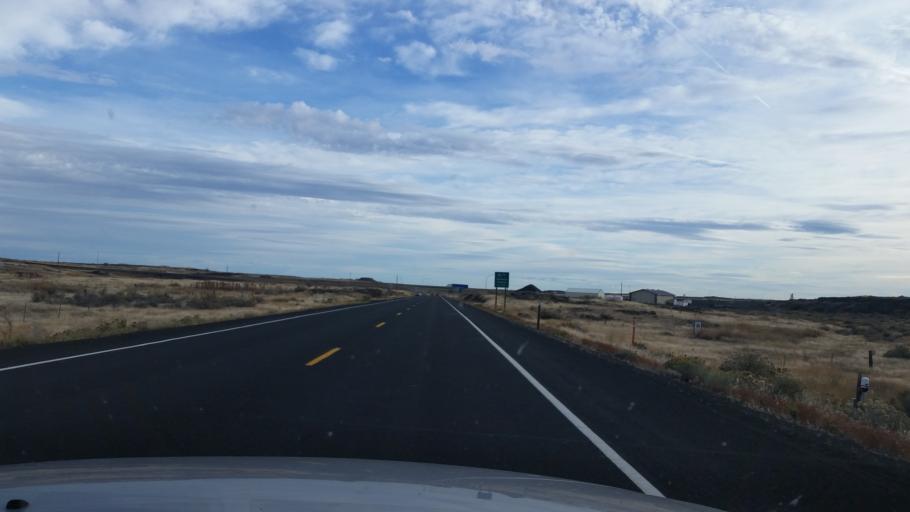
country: US
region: Washington
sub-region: Lincoln County
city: Davenport
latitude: 47.3141
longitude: -117.9736
